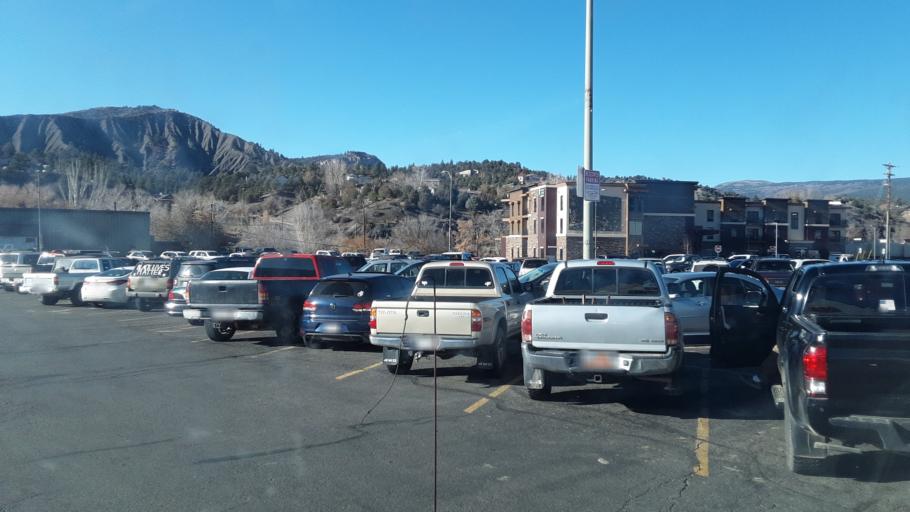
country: US
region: Colorado
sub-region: La Plata County
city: Durango
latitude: 37.2751
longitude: -107.8821
